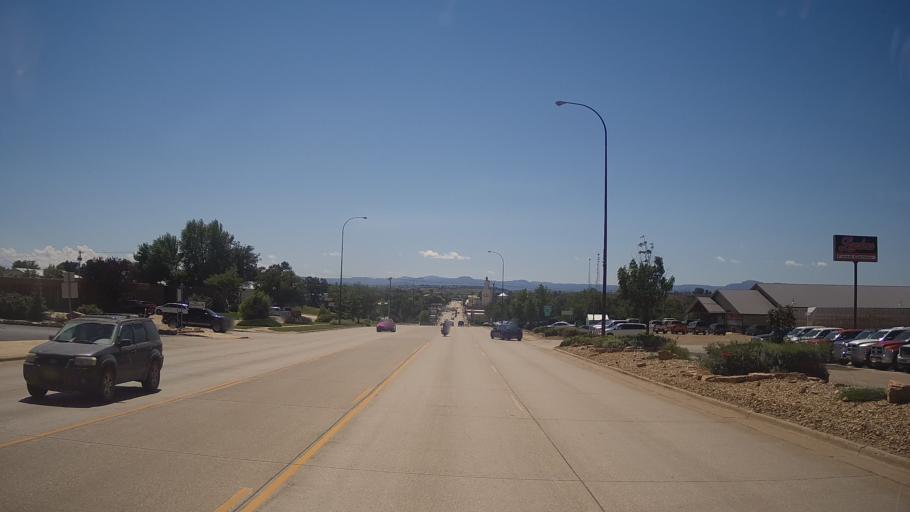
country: US
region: South Dakota
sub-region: Butte County
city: Belle Fourche
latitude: 44.6787
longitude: -103.8537
